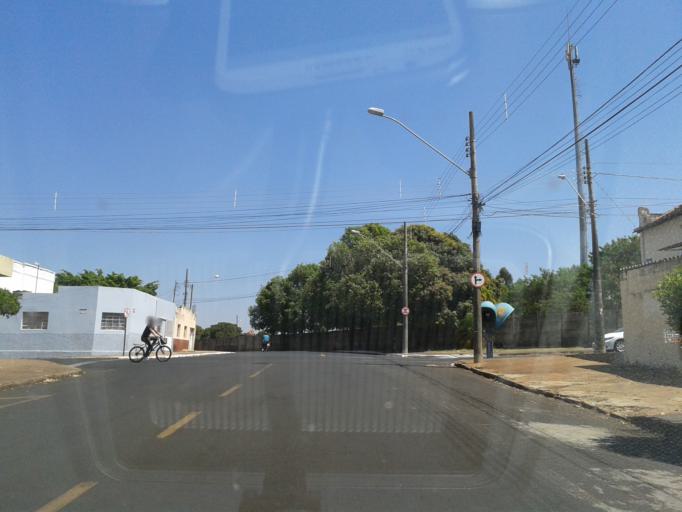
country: BR
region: Minas Gerais
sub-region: Araguari
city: Araguari
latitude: -18.6421
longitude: -48.1958
